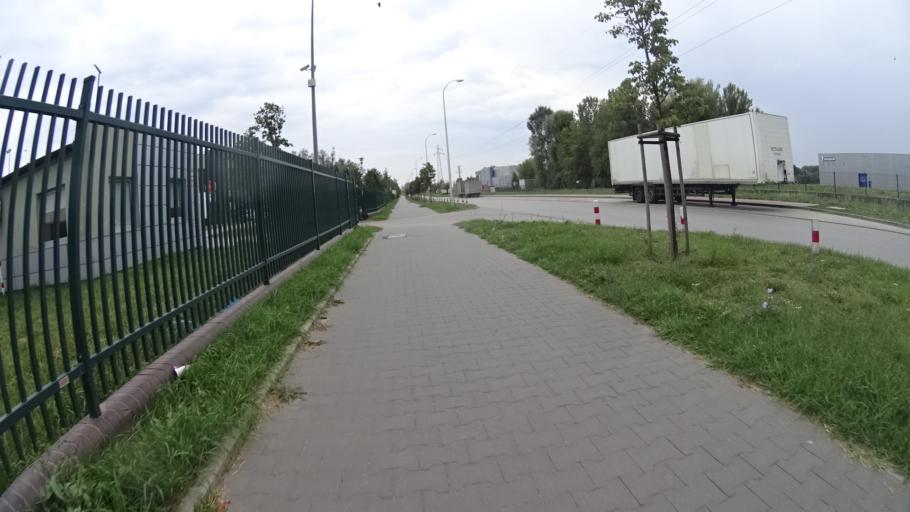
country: PL
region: Masovian Voivodeship
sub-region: Powiat pruszkowski
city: Otrebusy
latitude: 52.1652
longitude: 20.7678
